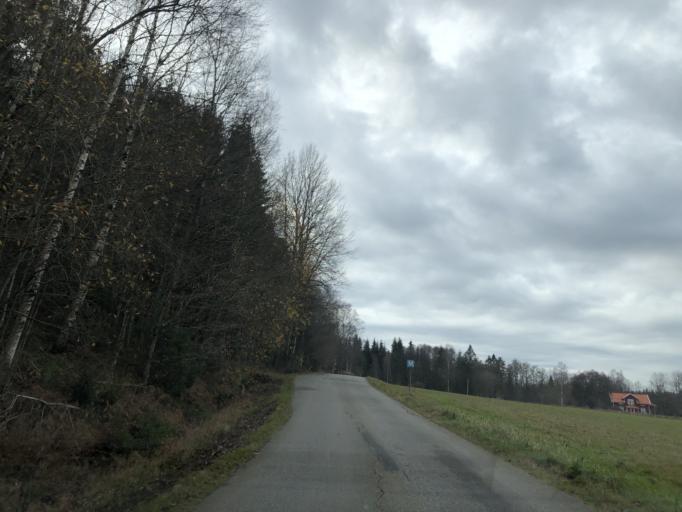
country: SE
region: Vaestra Goetaland
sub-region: Ulricehamns Kommun
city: Ulricehamn
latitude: 57.7253
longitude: 13.3596
